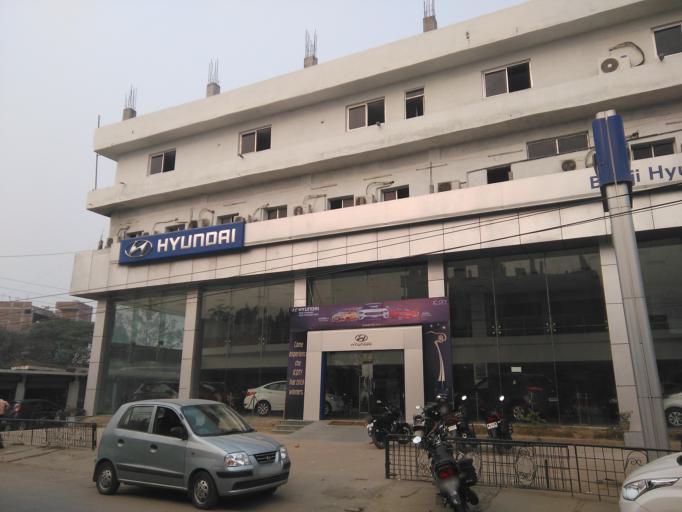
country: IN
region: Bihar
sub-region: Muzaffarpur
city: Muzaffarpur
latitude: 26.1088
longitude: 85.3872
